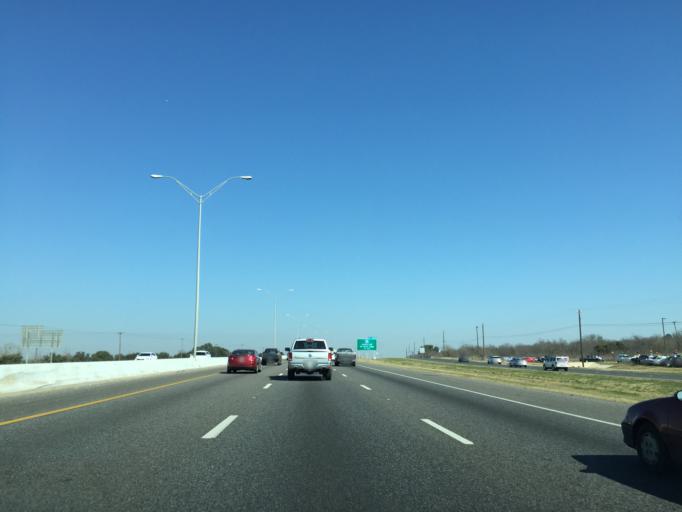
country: US
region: Texas
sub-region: Williamson County
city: Georgetown
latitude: 30.5830
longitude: -97.6929
